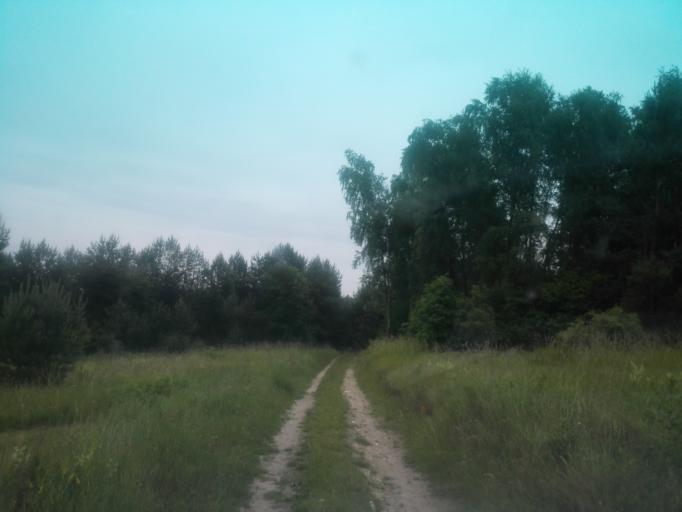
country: PL
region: Silesian Voivodeship
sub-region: Powiat czestochowski
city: Olsztyn
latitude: 50.7925
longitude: 19.2531
